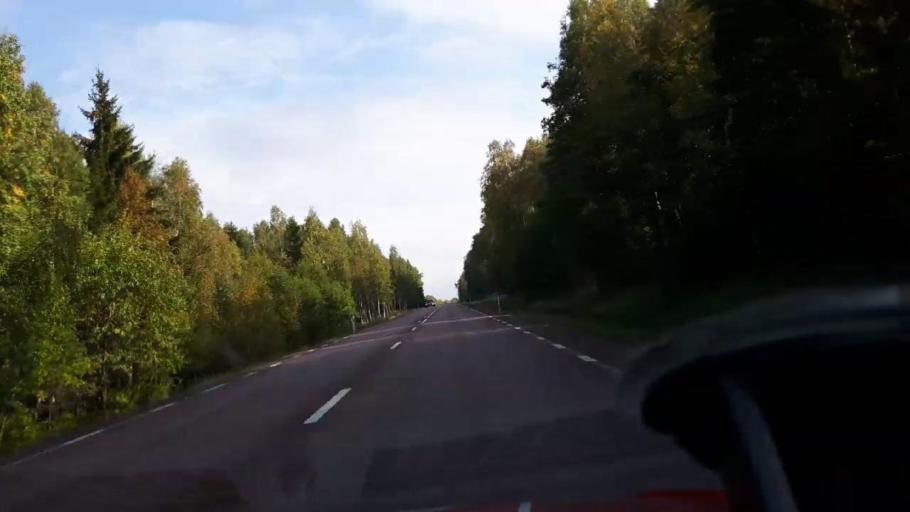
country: SE
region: Gaevleborg
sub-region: Bollnas Kommun
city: Kilafors
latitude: 61.2189
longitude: 16.6931
